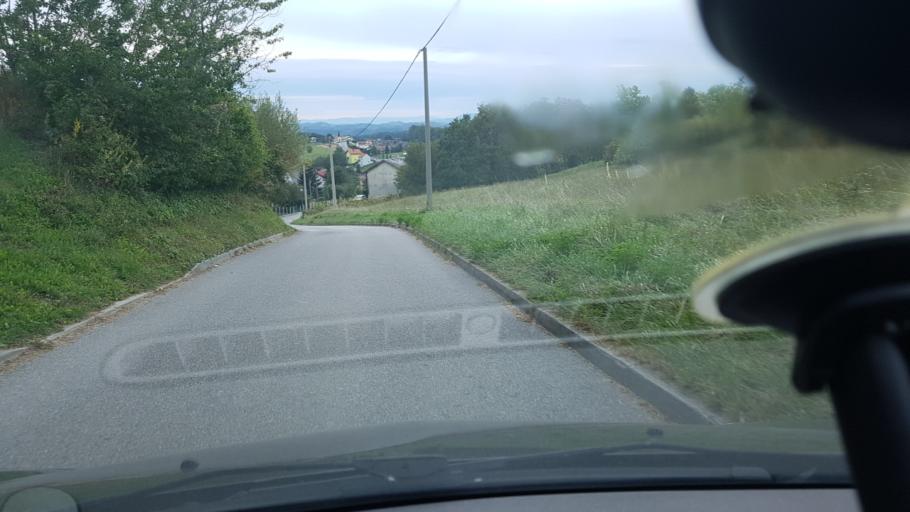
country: HR
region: Krapinsko-Zagorska
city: Radoboj
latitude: 46.1687
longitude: 15.9259
